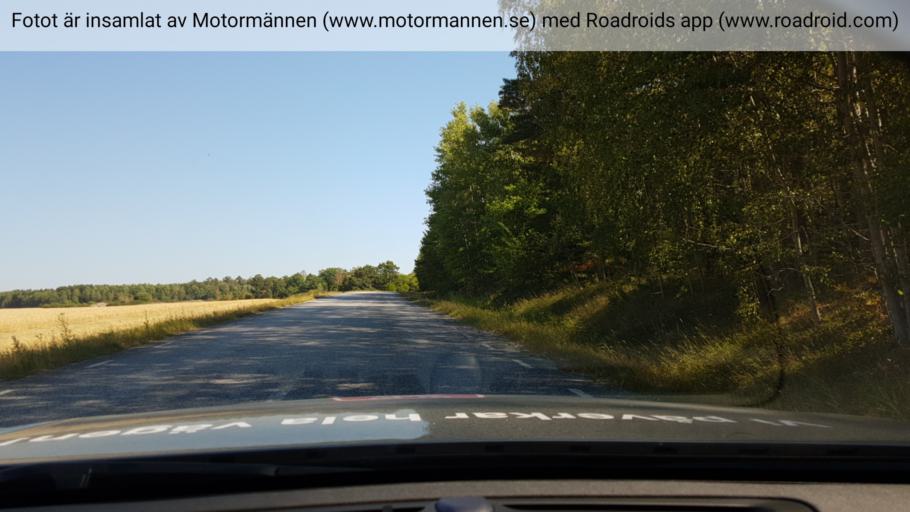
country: SE
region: Stockholm
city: Stenhamra
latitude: 59.3934
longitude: 17.5392
